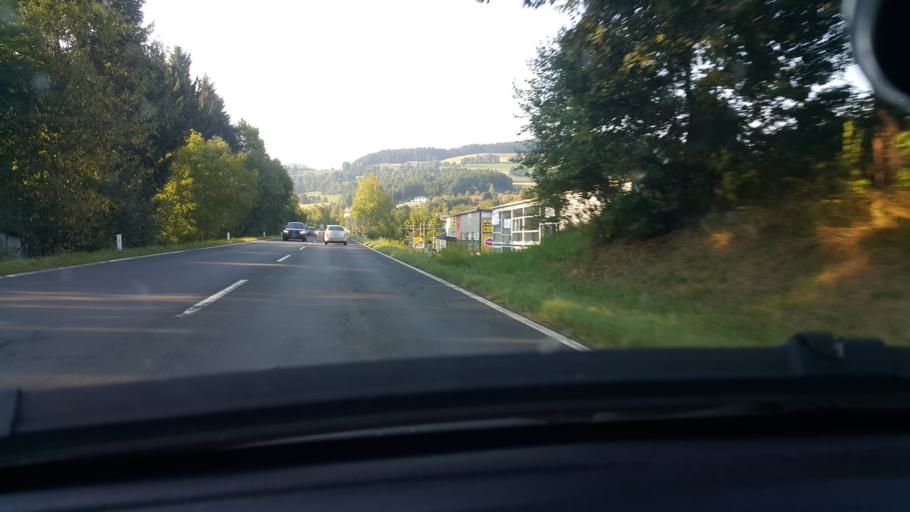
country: AT
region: Carinthia
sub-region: Politischer Bezirk Feldkirchen
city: Feldkirchen in Karnten
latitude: 46.7192
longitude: 14.1053
